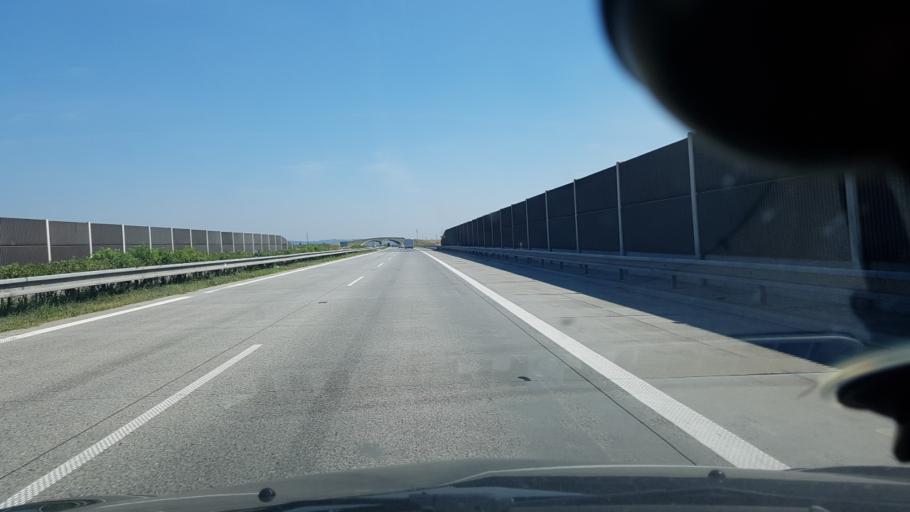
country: CZ
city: Fulnek
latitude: 49.6656
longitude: 17.9154
